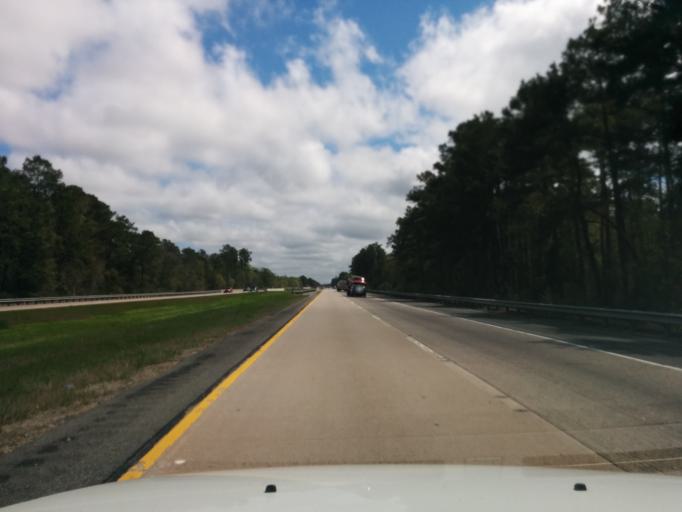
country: US
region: Georgia
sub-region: Chatham County
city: Bloomingdale
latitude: 32.1407
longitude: -81.4115
